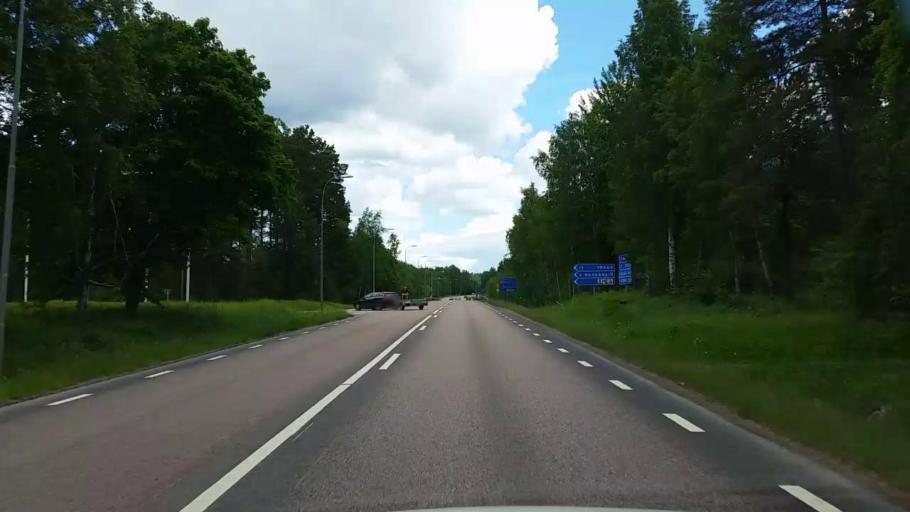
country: SE
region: Vaestmanland
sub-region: Norbergs Kommun
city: Norberg
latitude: 60.0714
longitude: 15.9196
